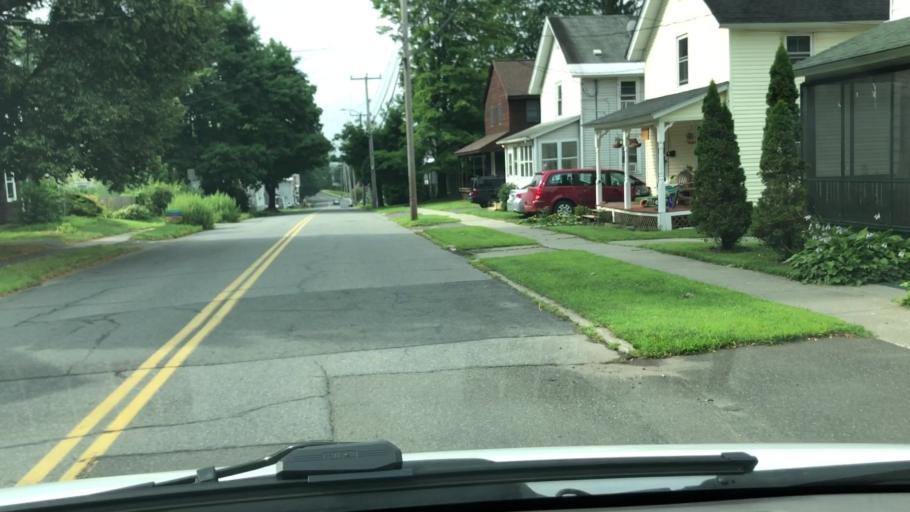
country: US
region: Massachusetts
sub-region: Franklin County
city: Greenfield
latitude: 42.5949
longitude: -72.6043
